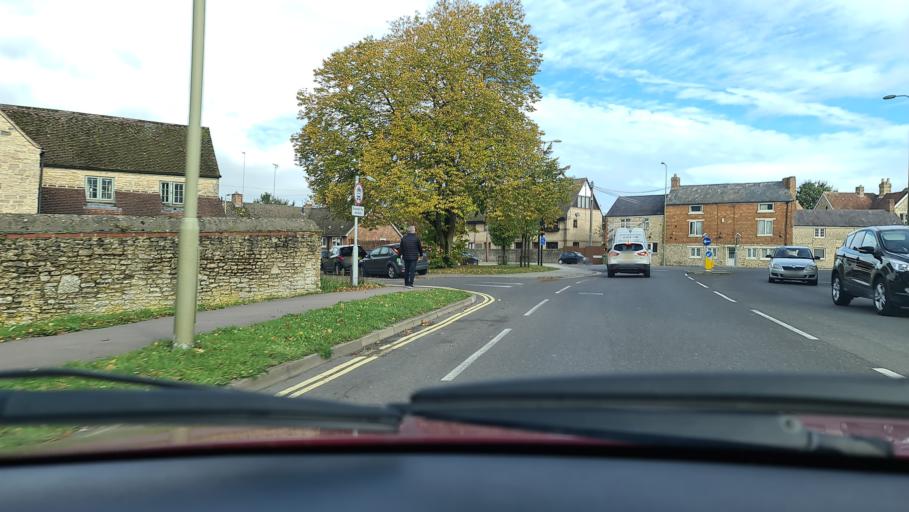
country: GB
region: England
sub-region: Oxfordshire
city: Bicester
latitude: 51.8994
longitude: -1.1542
